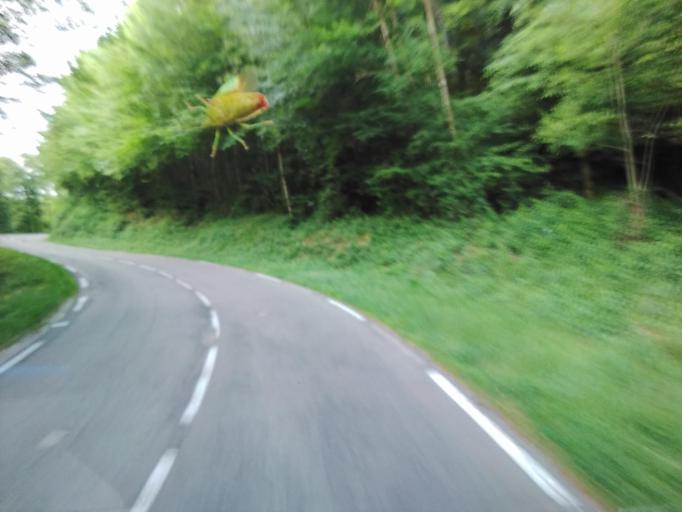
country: FR
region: Franche-Comte
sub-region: Departement du Jura
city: Arbois
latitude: 46.8872
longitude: 5.7999
